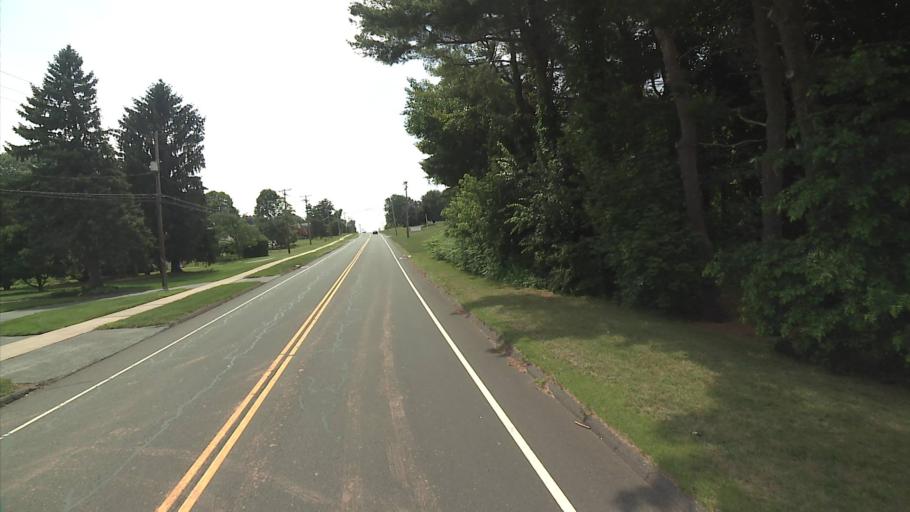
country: US
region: Connecticut
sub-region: Hartford County
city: Newington
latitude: 41.6747
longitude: -72.7331
